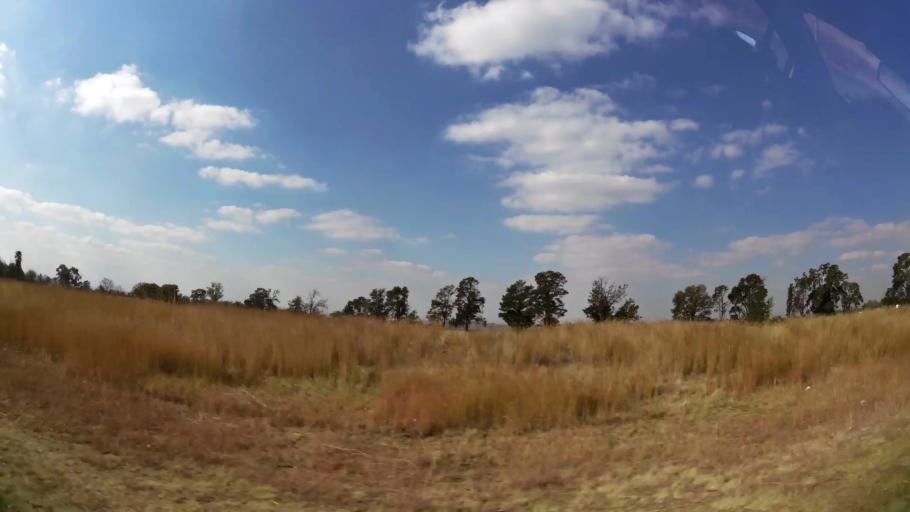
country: ZA
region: Gauteng
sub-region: West Rand District Municipality
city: Krugersdorp
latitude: -26.0656
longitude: 27.7613
